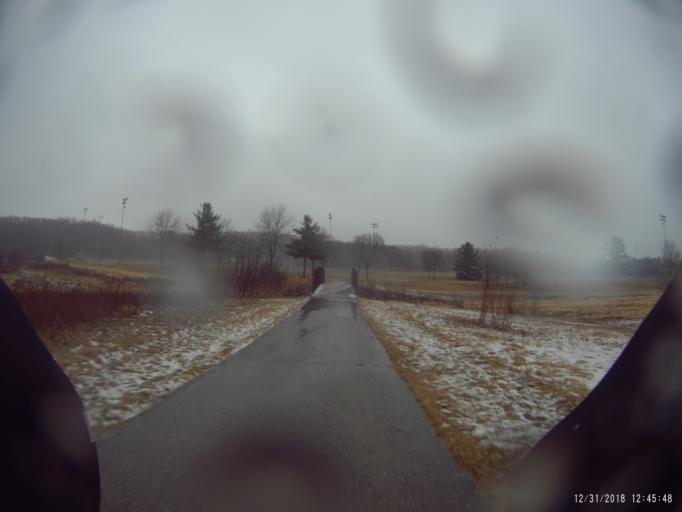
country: US
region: Wisconsin
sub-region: Dane County
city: Verona
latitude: 43.0364
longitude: -89.5089
